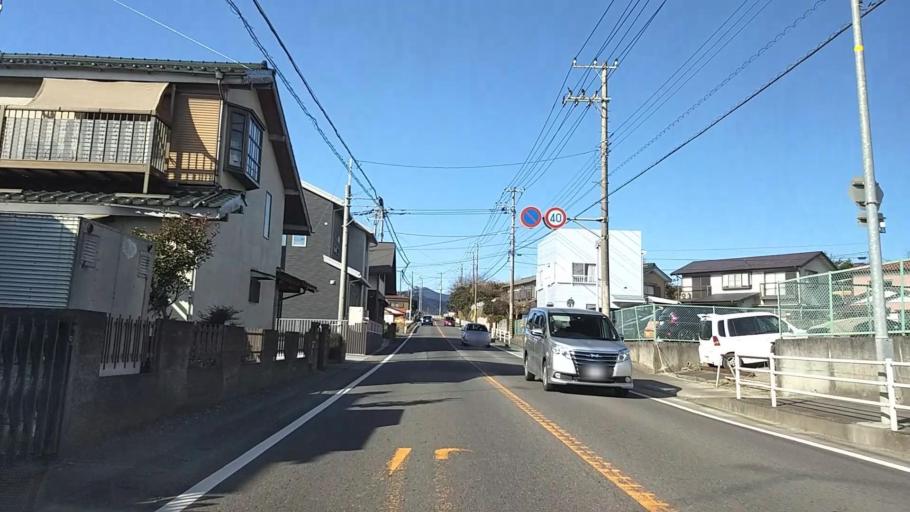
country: JP
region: Kanagawa
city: Atsugi
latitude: 35.4680
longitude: 139.3330
